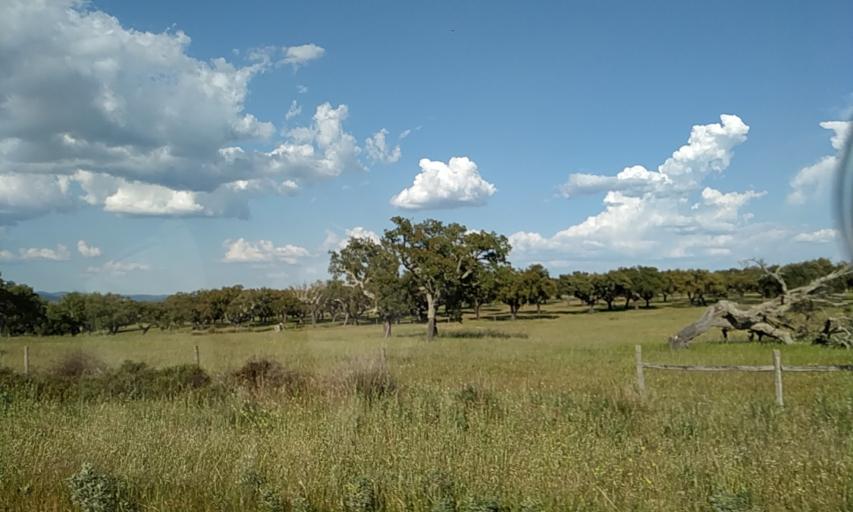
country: PT
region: Portalegre
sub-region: Portalegre
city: Urra
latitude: 39.1542
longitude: -7.4543
